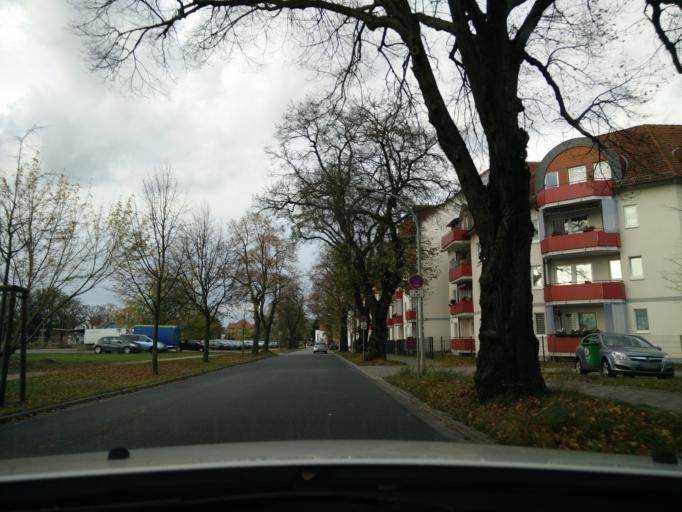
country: DE
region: Brandenburg
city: Velten
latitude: 52.6839
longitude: 13.1748
